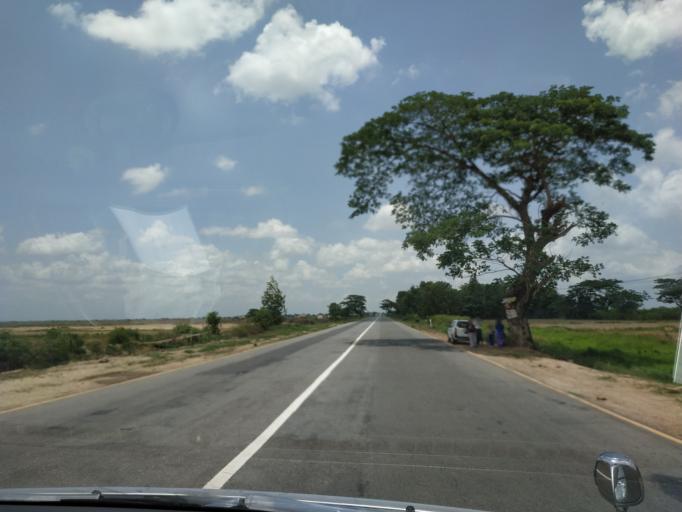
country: MM
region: Bago
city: Bago
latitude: 17.4616
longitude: 96.5954
